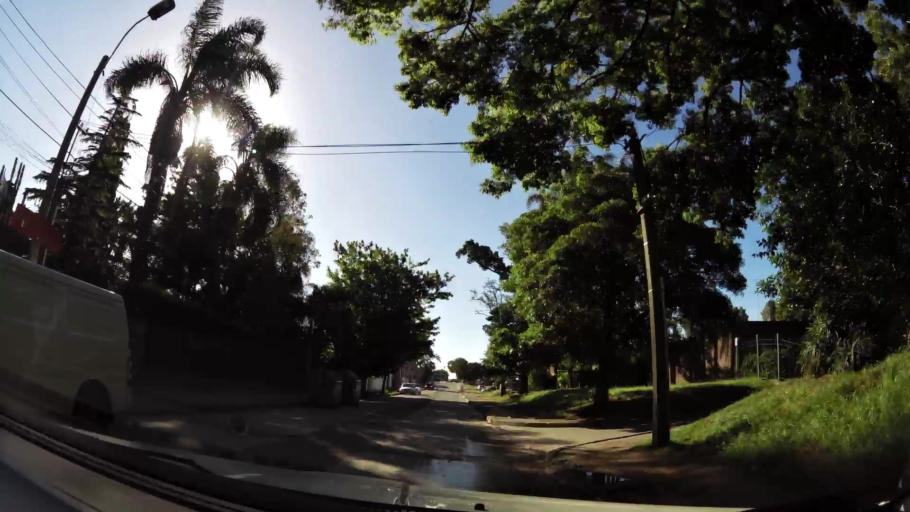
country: UY
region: Montevideo
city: Montevideo
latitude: -34.8466
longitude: -56.2209
